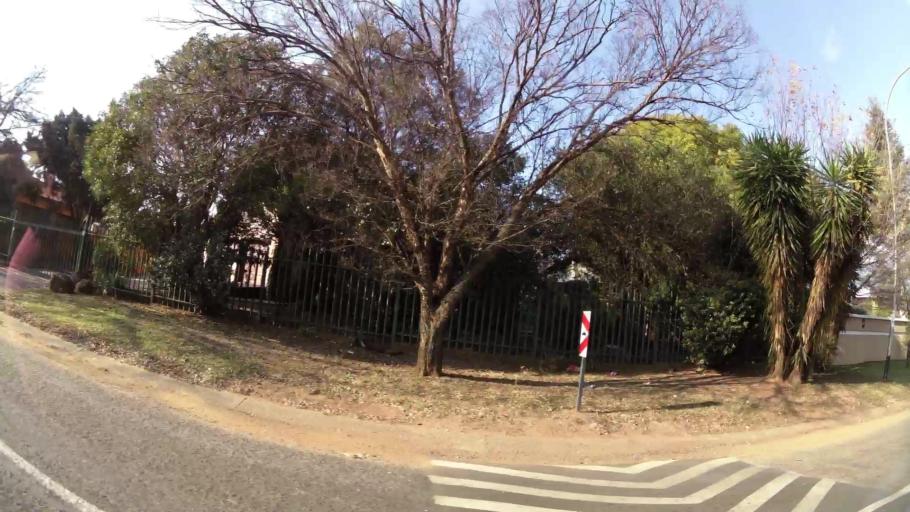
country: ZA
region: Gauteng
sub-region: Ekurhuleni Metropolitan Municipality
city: Tembisa
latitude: -25.9568
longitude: 28.2181
